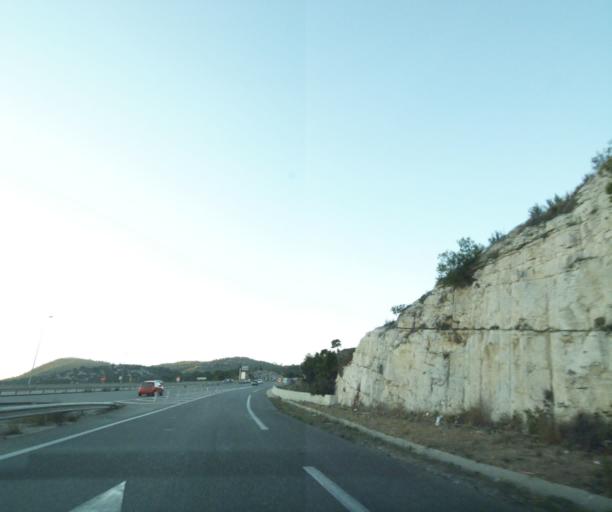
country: FR
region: Provence-Alpes-Cote d'Azur
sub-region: Departement des Bouches-du-Rhone
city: La Ciotat
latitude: 43.2065
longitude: 5.5883
